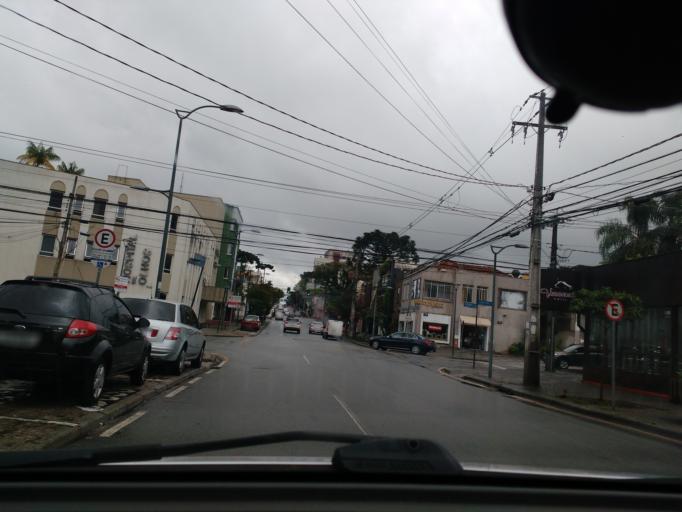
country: BR
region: Parana
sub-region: Curitiba
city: Curitiba
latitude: -25.4351
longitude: -49.2852
